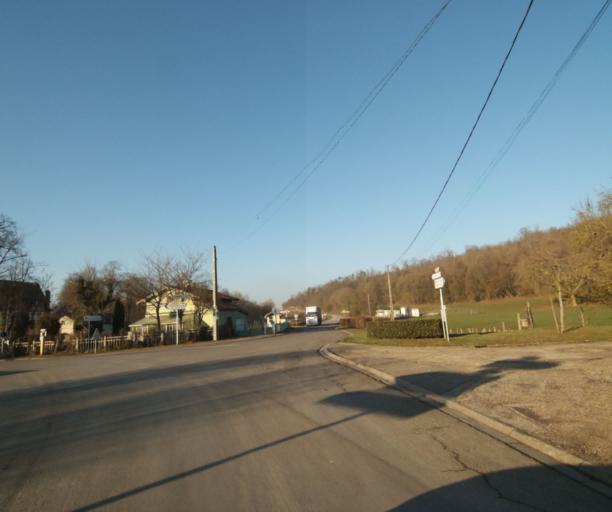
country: FR
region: Champagne-Ardenne
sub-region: Departement de la Haute-Marne
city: Bienville
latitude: 48.5834
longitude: 5.0453
